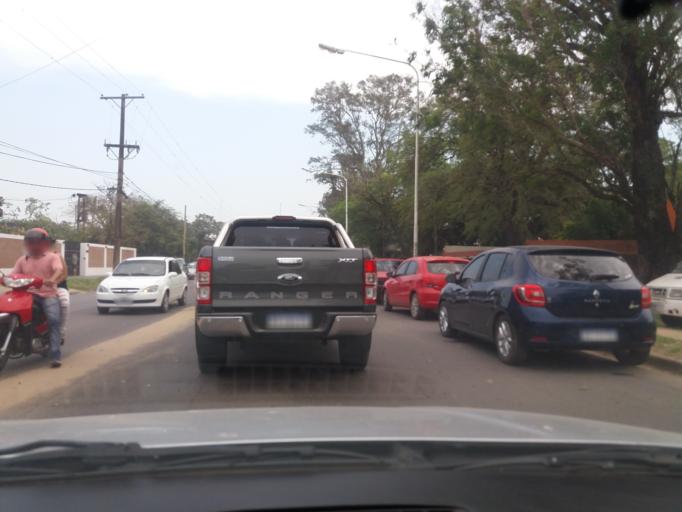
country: AR
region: Corrientes
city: Corrientes
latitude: -27.5058
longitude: -58.8111
